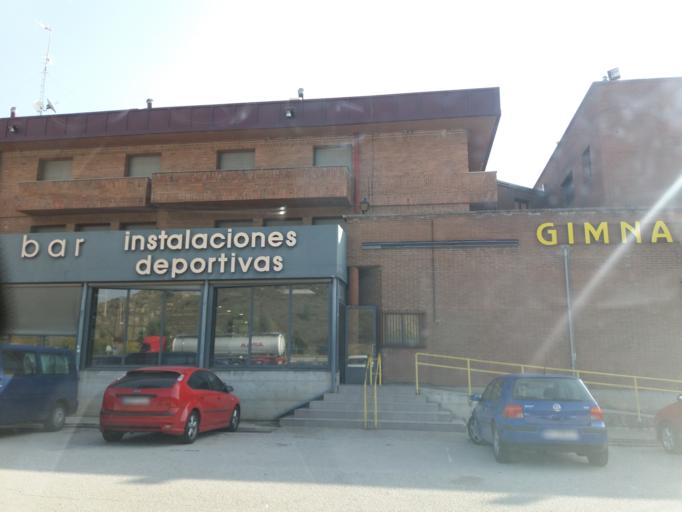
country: ES
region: Navarre
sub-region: Provincia de Navarra
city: Liedena
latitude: 42.6134
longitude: -1.2777
